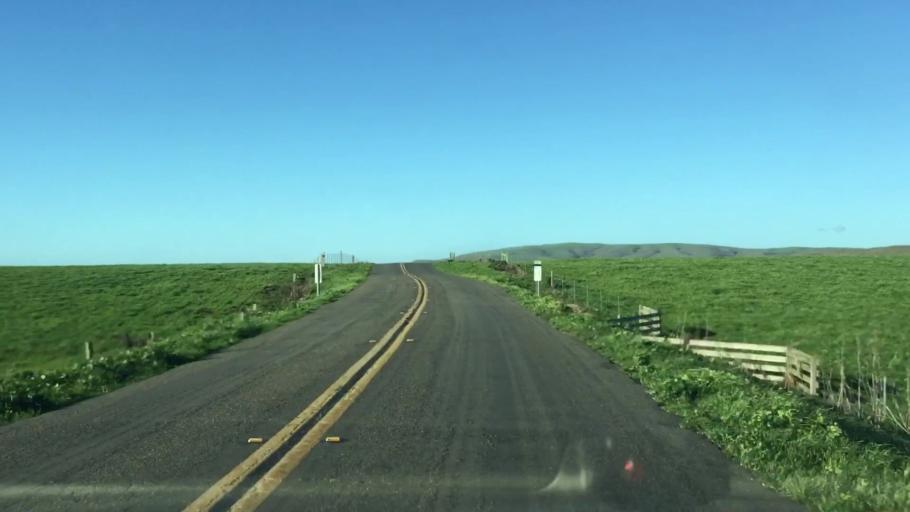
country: US
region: California
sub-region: Marin County
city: Inverness
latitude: 38.1347
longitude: -122.9347
